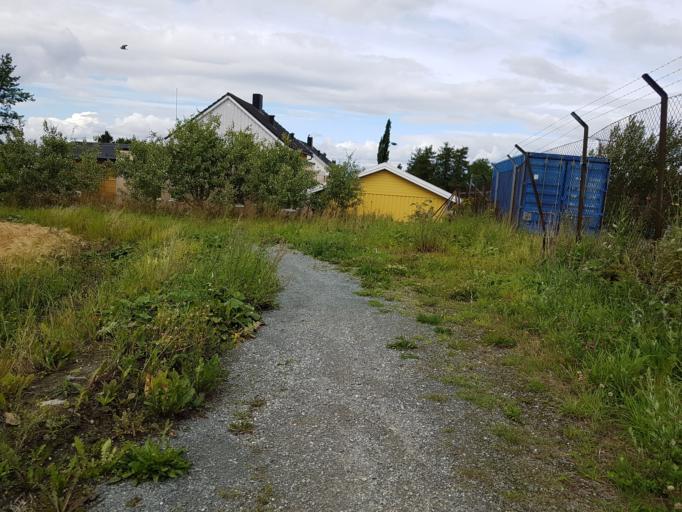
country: NO
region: Sor-Trondelag
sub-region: Trondheim
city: Trondheim
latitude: 63.4227
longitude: 10.4607
